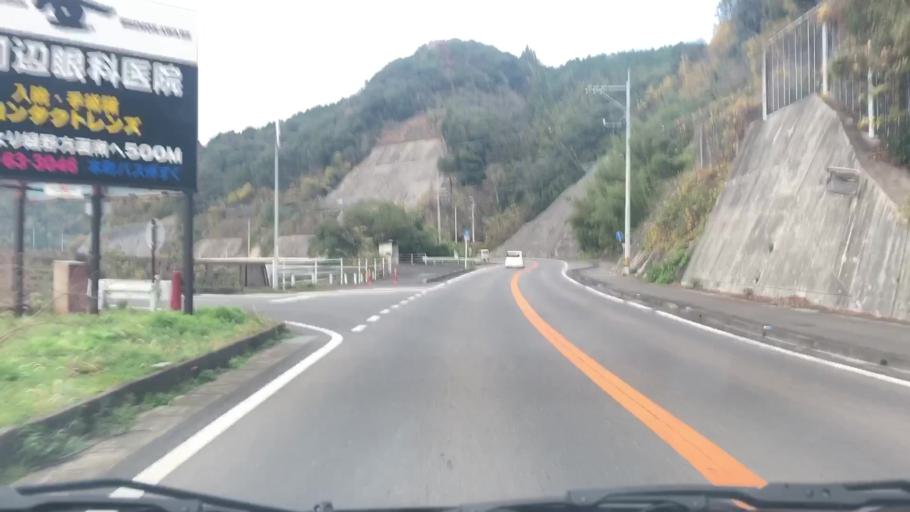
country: JP
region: Saga Prefecture
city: Ureshinomachi-shimojuku
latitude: 33.1360
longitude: 130.0252
